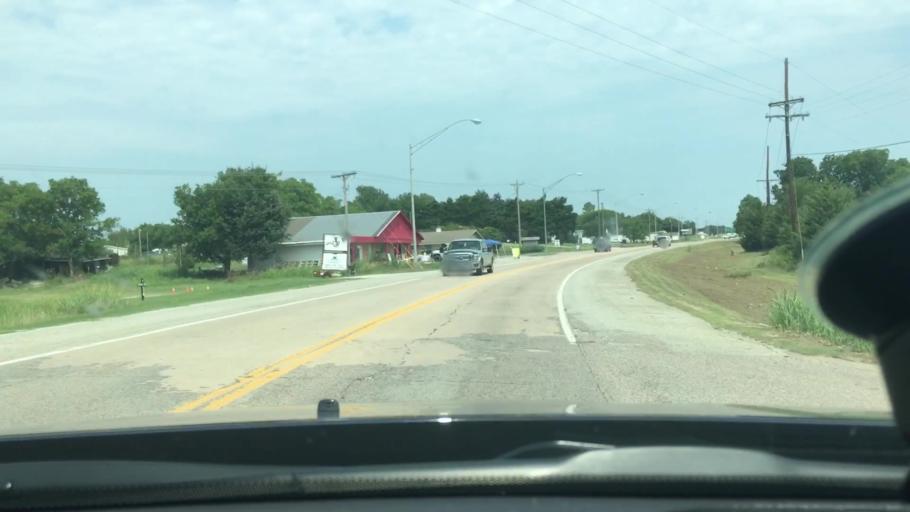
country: US
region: Oklahoma
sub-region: Marshall County
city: Kingston
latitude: 34.0017
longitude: -96.7260
